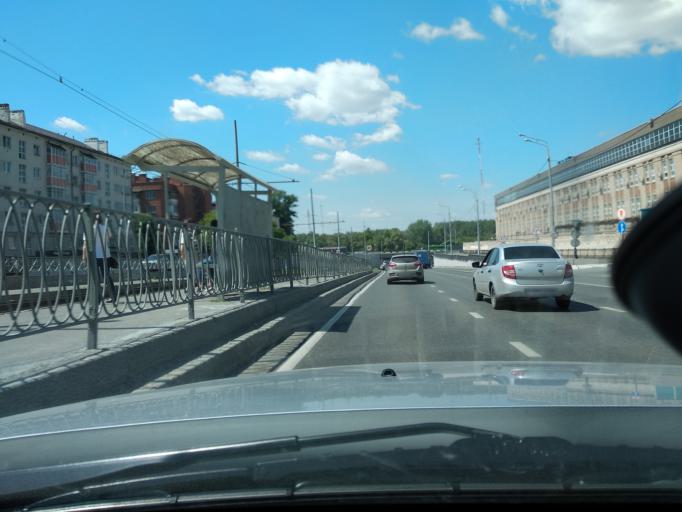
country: RU
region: Tatarstan
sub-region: Gorod Kazan'
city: Kazan
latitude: 55.8149
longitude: 49.1845
